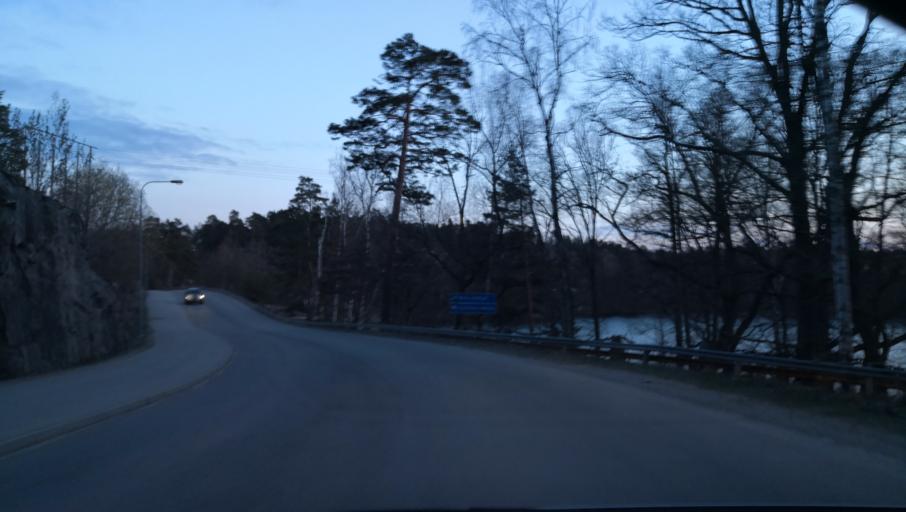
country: SE
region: Stockholm
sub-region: Nacka Kommun
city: Boo
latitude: 59.3377
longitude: 18.2950
